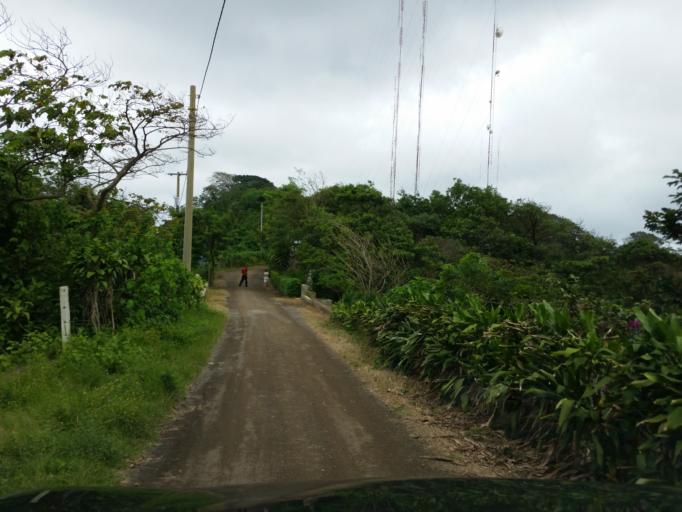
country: NI
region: Managua
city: El Crucero
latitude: 12.0129
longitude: -86.2731
